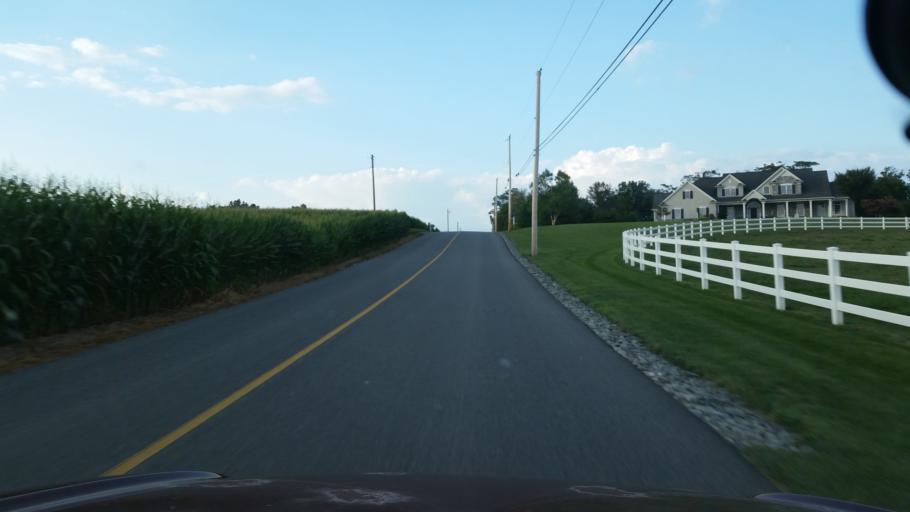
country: US
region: Pennsylvania
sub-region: Lancaster County
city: Mount Joy
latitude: 40.1507
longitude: -76.4631
